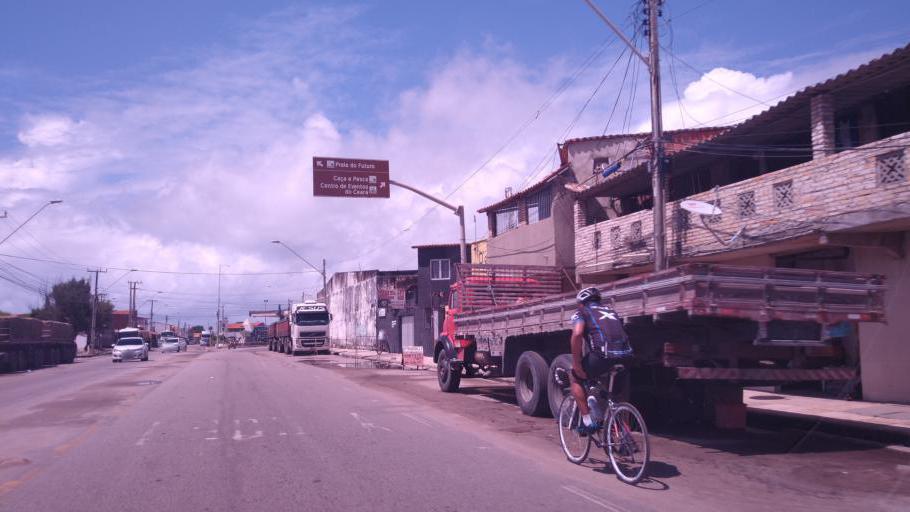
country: BR
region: Ceara
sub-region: Fortaleza
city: Fortaleza
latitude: -3.7180
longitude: -38.4663
